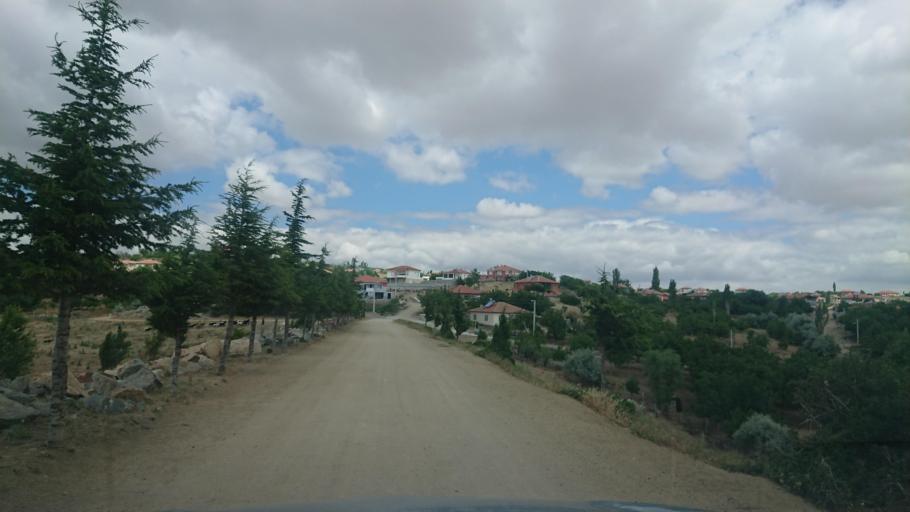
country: TR
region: Aksaray
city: Agacoren
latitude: 38.8661
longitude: 33.9494
